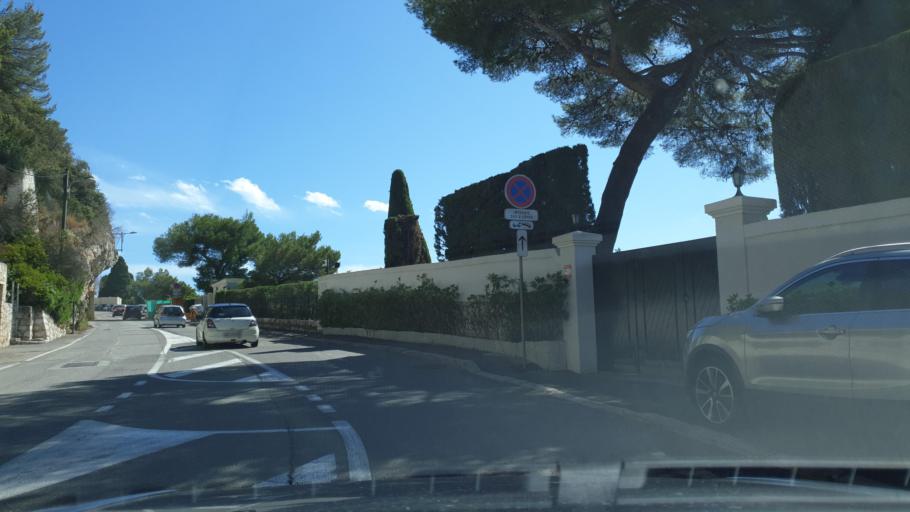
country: FR
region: Provence-Alpes-Cote d'Azur
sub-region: Departement des Alpes-Maritimes
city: Eze
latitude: 43.7197
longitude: 7.3708
